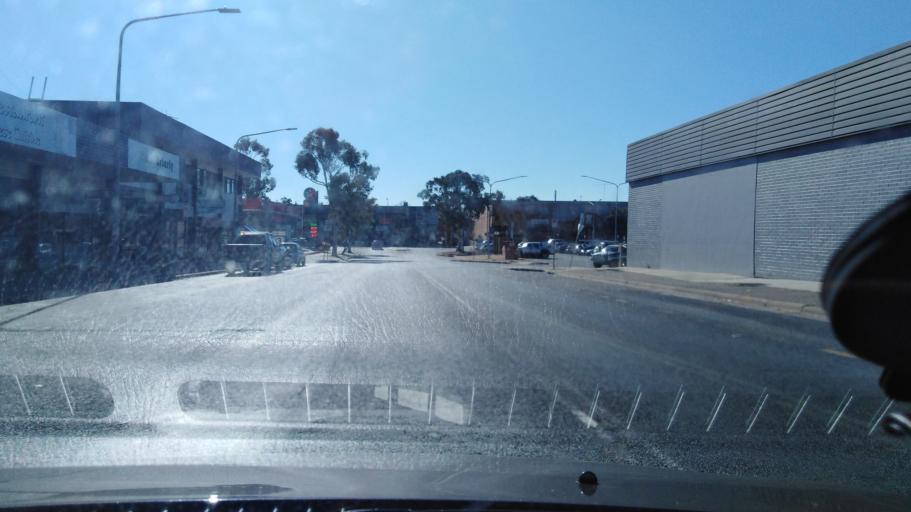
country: AU
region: Australian Capital Territory
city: Forrest
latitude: -35.3410
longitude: 149.0523
